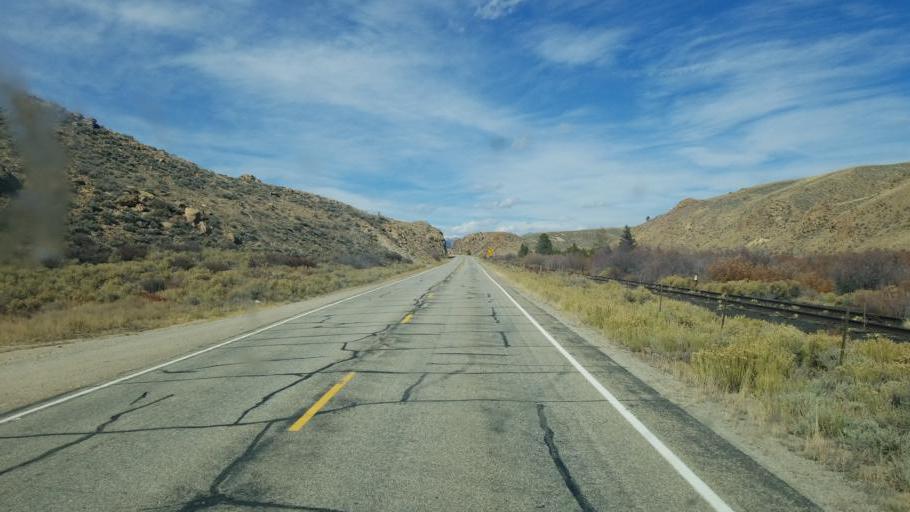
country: US
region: Colorado
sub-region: Lake County
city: Leadville
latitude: 39.0985
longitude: -106.2922
